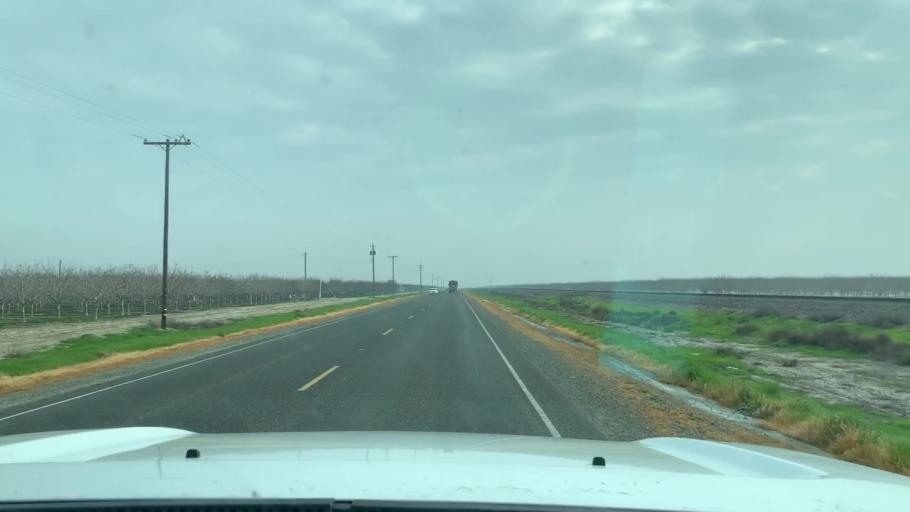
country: US
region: California
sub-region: Tulare County
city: Earlimart
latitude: 35.8277
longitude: -119.3681
